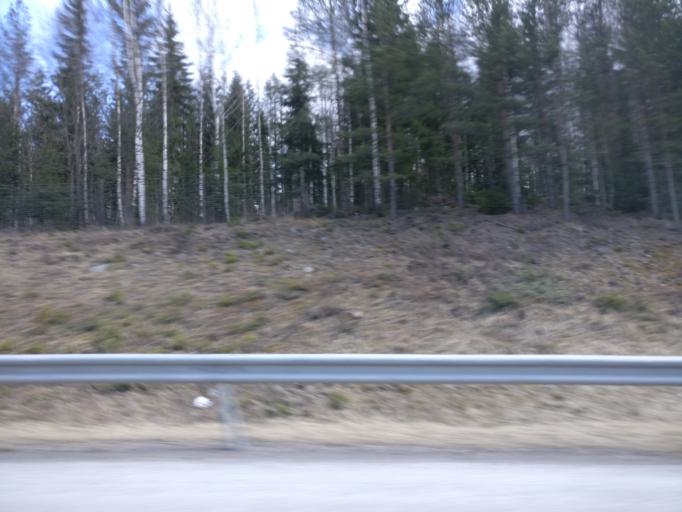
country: FI
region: Haeme
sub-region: Riihimaeki
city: Riihimaeki
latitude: 60.7472
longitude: 24.7302
